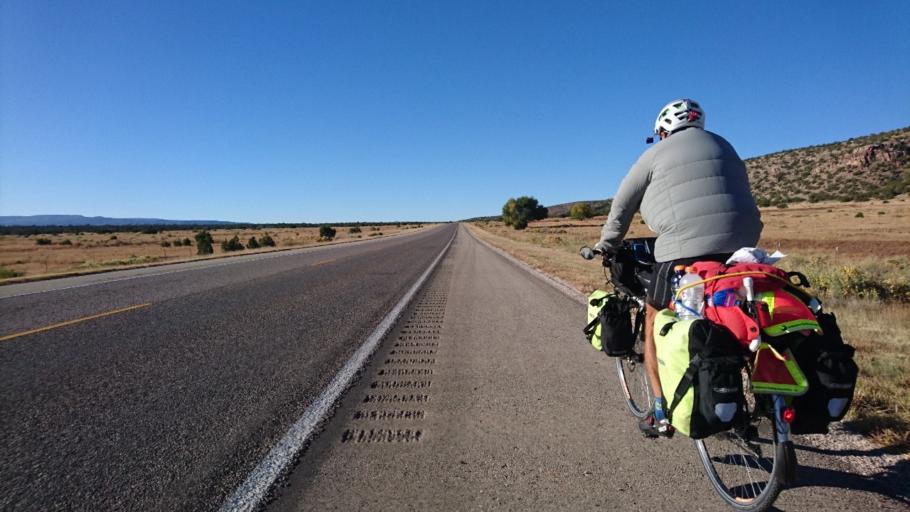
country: US
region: New Mexico
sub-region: Cibola County
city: Grants
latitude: 34.9909
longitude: -107.9007
